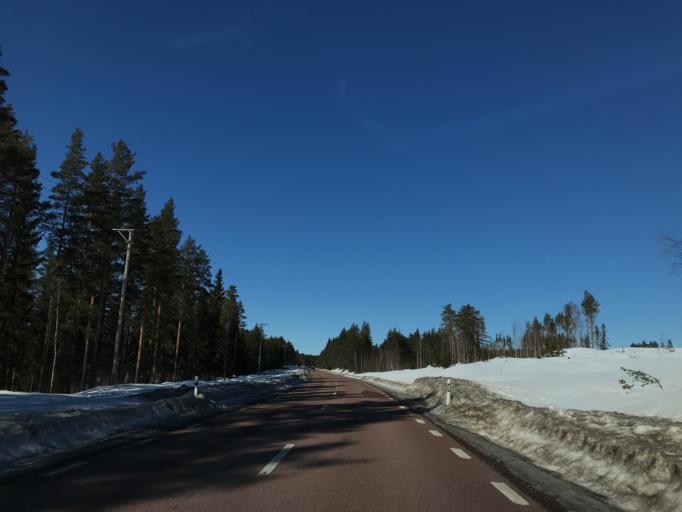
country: SE
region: Vaermland
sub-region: Filipstads Kommun
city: Lesjofors
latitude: 60.1637
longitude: 14.2041
